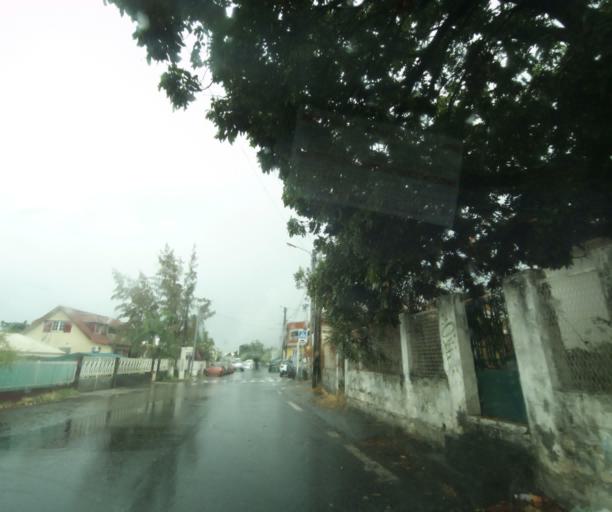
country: RE
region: Reunion
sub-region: Reunion
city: La Possession
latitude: -20.9817
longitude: 55.3272
